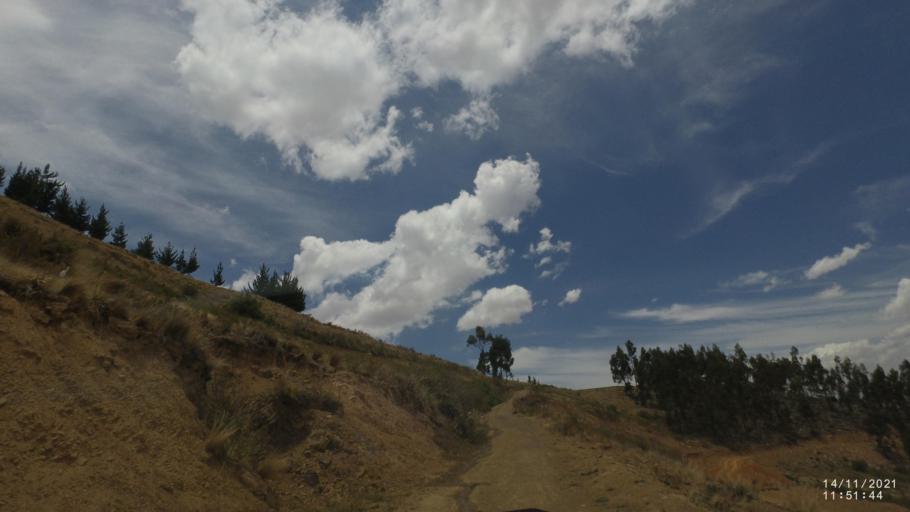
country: BO
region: Cochabamba
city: Colomi
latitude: -17.3611
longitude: -65.9827
